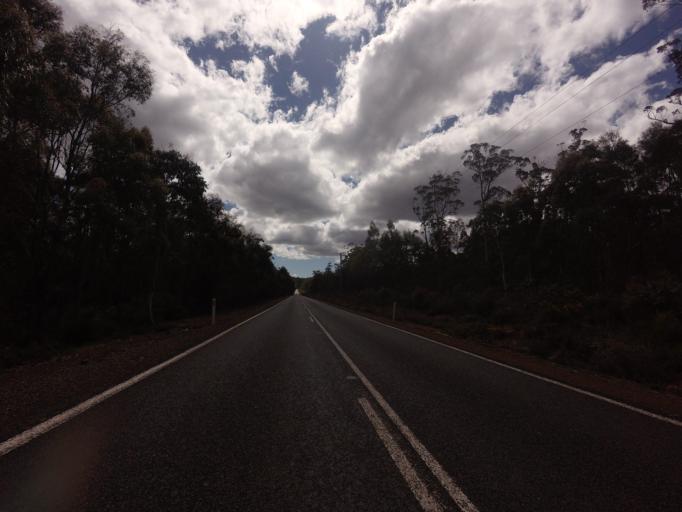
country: AU
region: Tasmania
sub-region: Northern Midlands
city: Evandale
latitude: -42.0234
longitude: 147.7498
